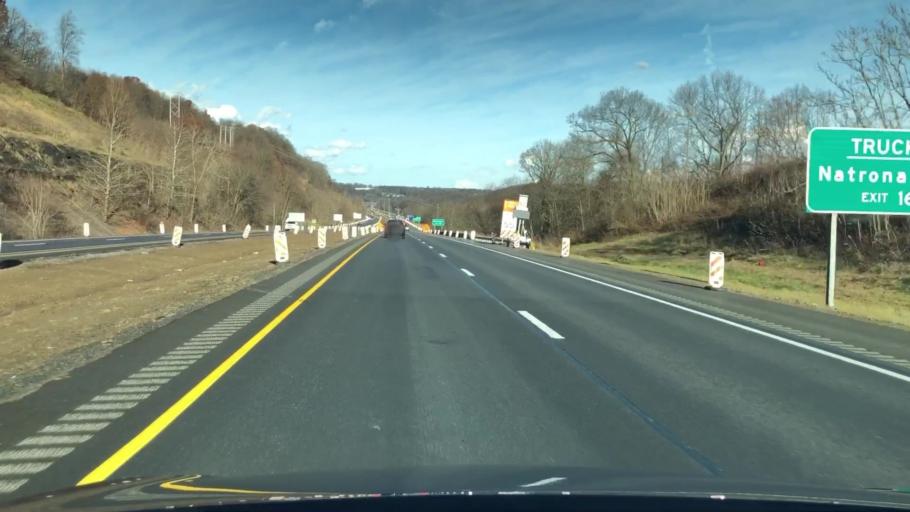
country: US
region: Pennsylvania
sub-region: Allegheny County
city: Brackenridge
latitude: 40.6211
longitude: -79.7460
